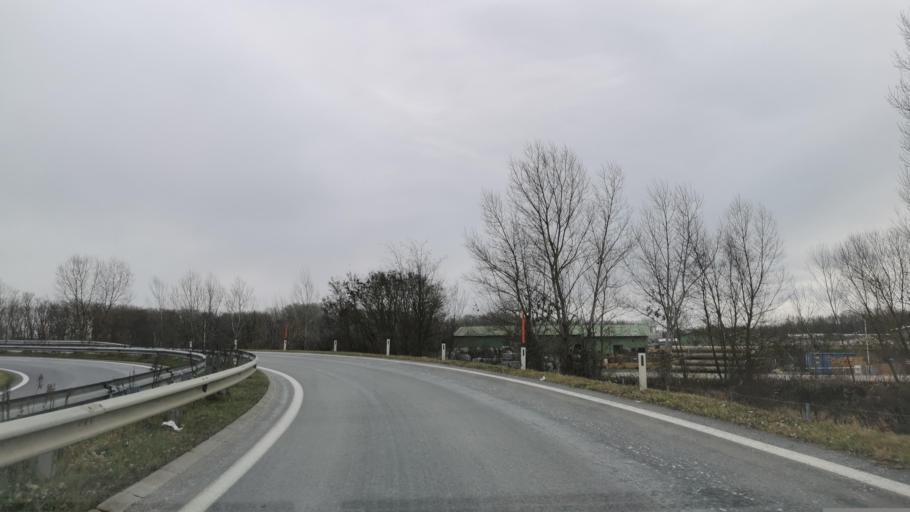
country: AT
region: Lower Austria
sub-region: Politischer Bezirk Krems
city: Gedersdorf
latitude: 48.4030
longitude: 15.6594
